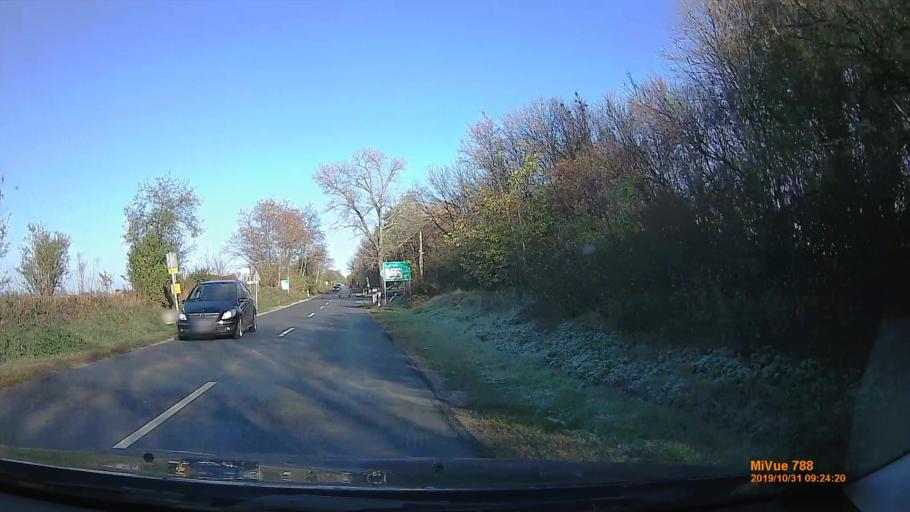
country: HU
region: Pest
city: Maglod
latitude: 47.4329
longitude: 19.3791
